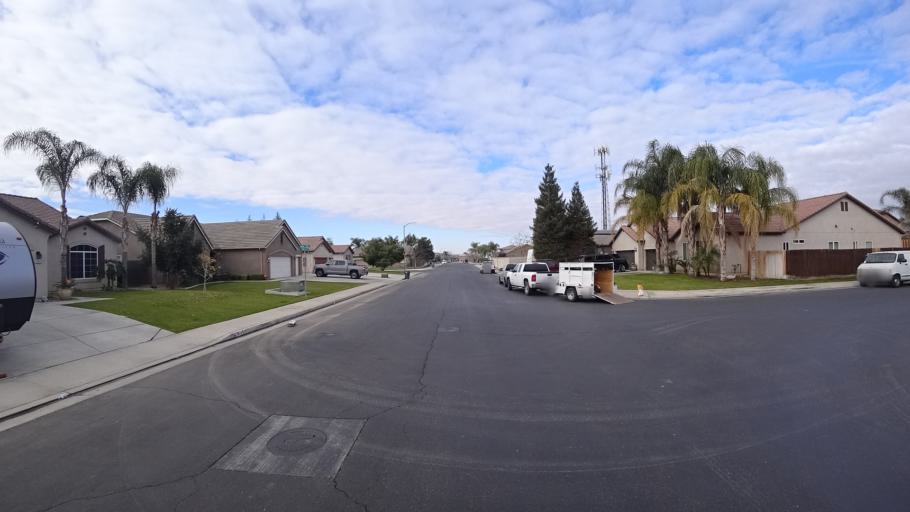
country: US
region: California
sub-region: Kern County
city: Rosedale
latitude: 35.2994
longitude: -119.1312
